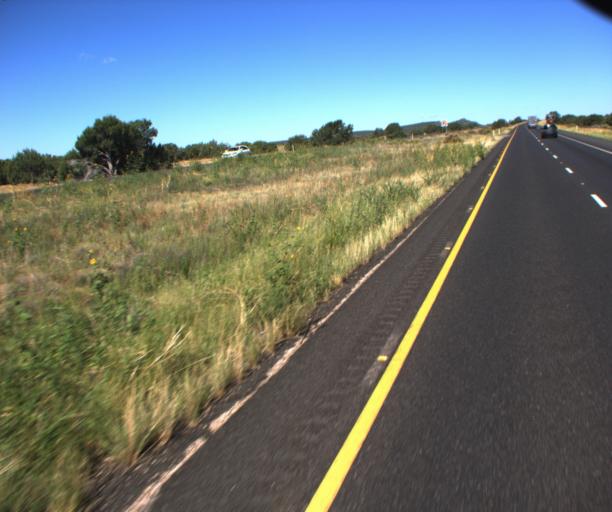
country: US
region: Arizona
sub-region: Yavapai County
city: Paulden
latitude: 35.2567
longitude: -112.7081
